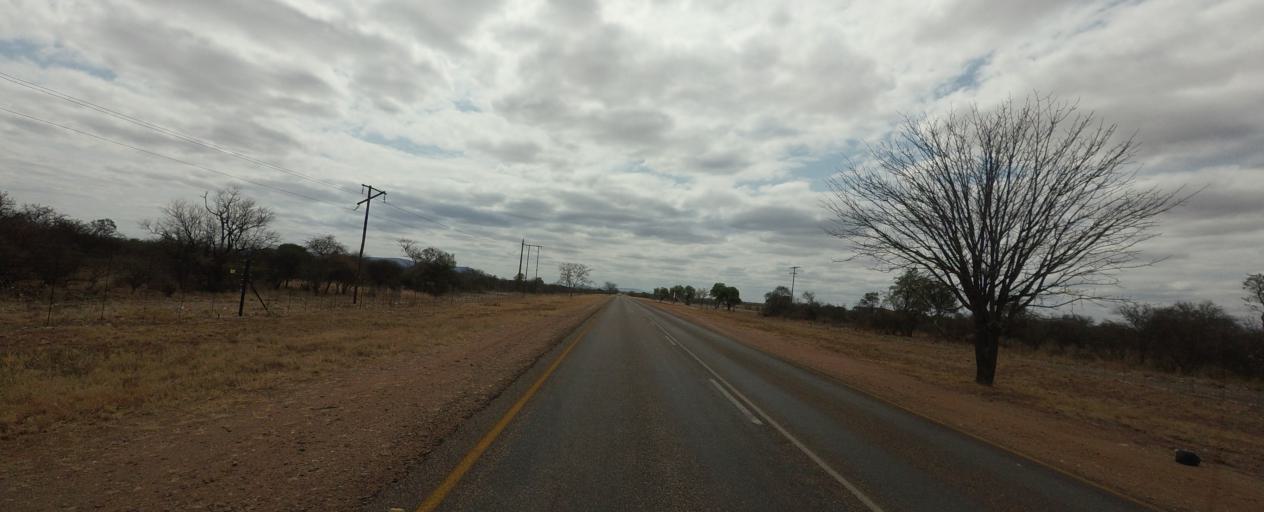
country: BW
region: Central
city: Makobeng
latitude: -23.0411
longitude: 27.9771
